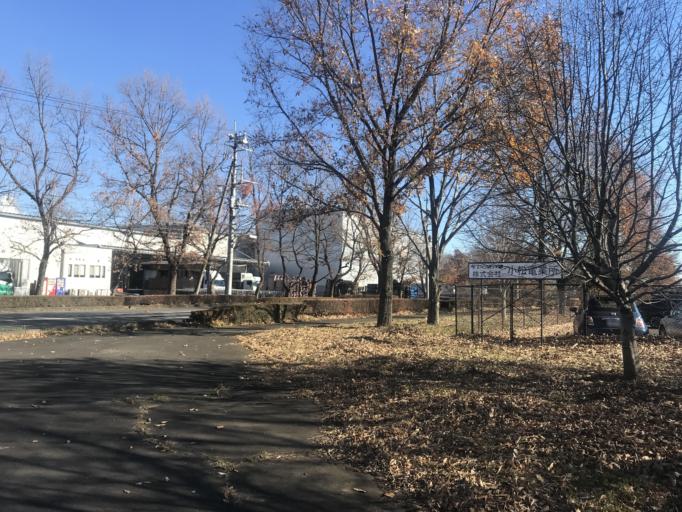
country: JP
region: Ibaraki
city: Yuki
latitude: 36.3286
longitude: 139.8799
